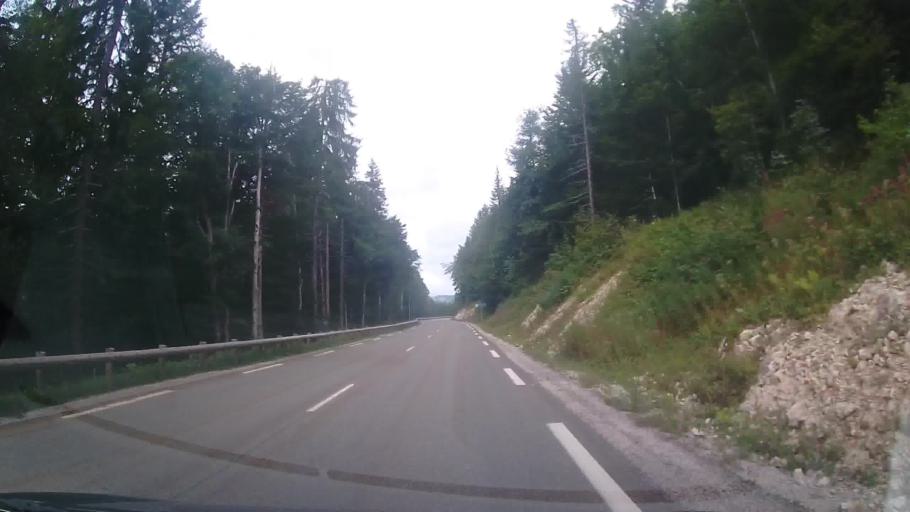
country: FR
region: Franche-Comte
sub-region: Departement du Jura
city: Les Rousses
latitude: 46.4257
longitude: 6.0694
